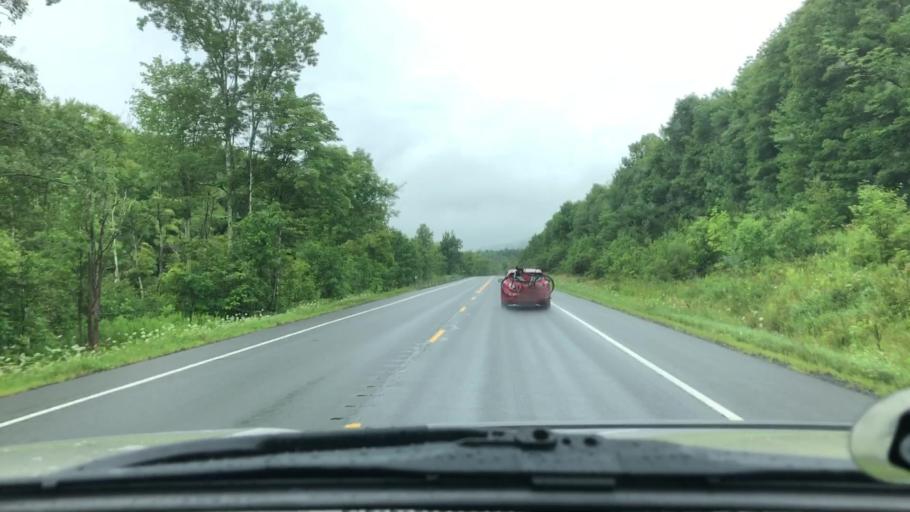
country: US
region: New York
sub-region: Greene County
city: Cairo
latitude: 42.3175
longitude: -74.1825
